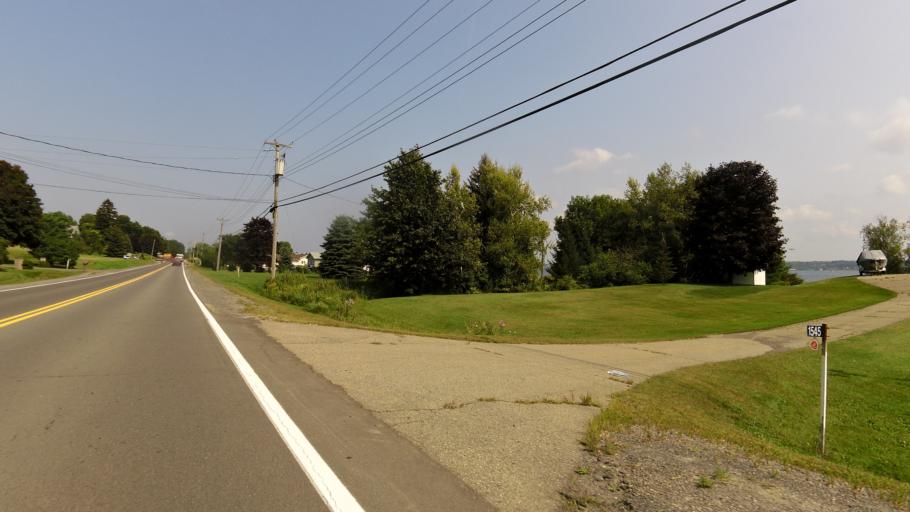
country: CA
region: Ontario
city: Prescott
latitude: 44.6857
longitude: -75.5535
